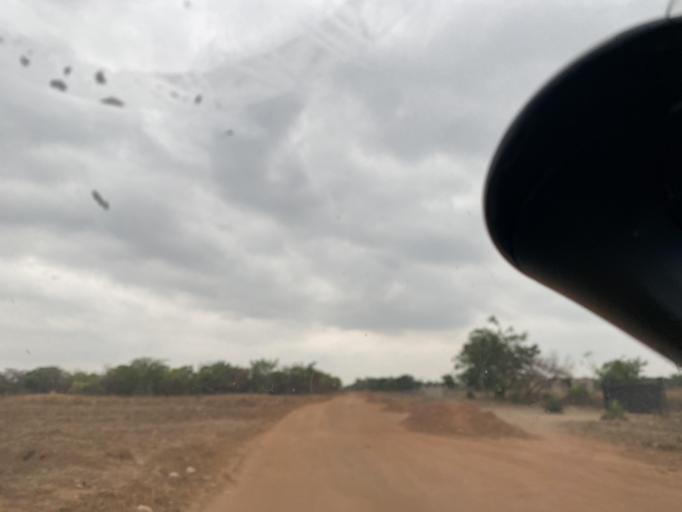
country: ZM
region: Lusaka
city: Chongwe
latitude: -15.2763
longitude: 28.7304
